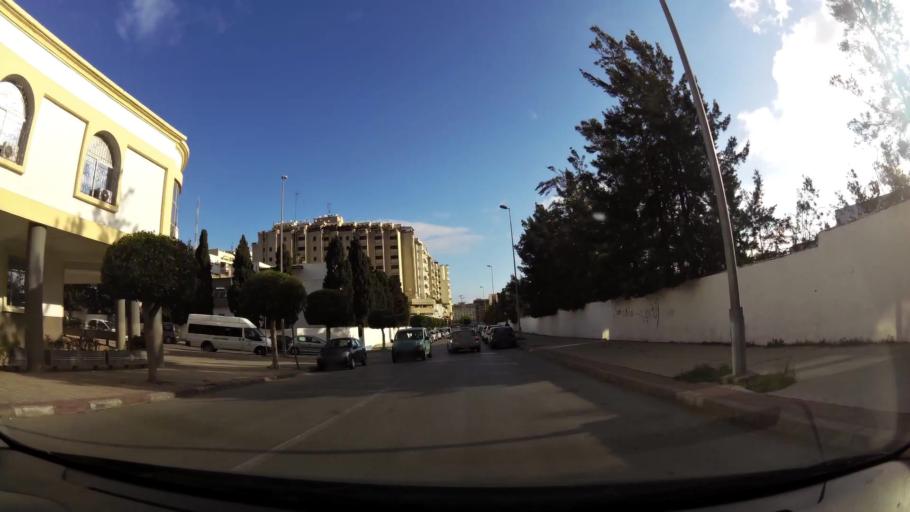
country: MA
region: Tanger-Tetouan
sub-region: Tanger-Assilah
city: Tangier
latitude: 35.7737
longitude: -5.8056
